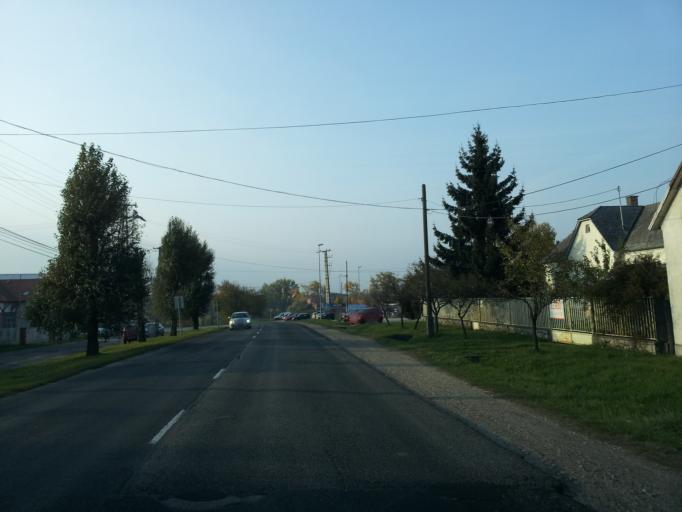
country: HU
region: Komarom-Esztergom
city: Kisber
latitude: 47.5086
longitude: 18.0118
